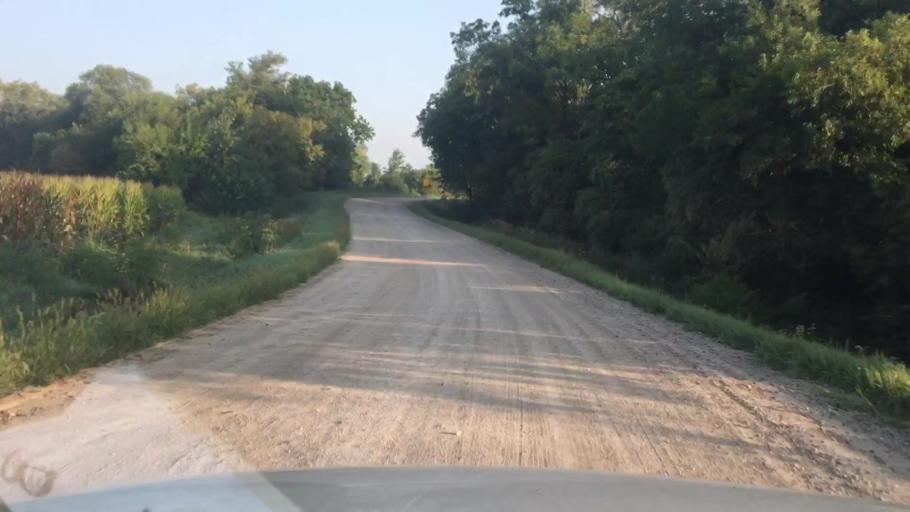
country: US
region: Iowa
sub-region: Story County
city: Huxley
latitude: 41.8915
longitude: -93.5811
